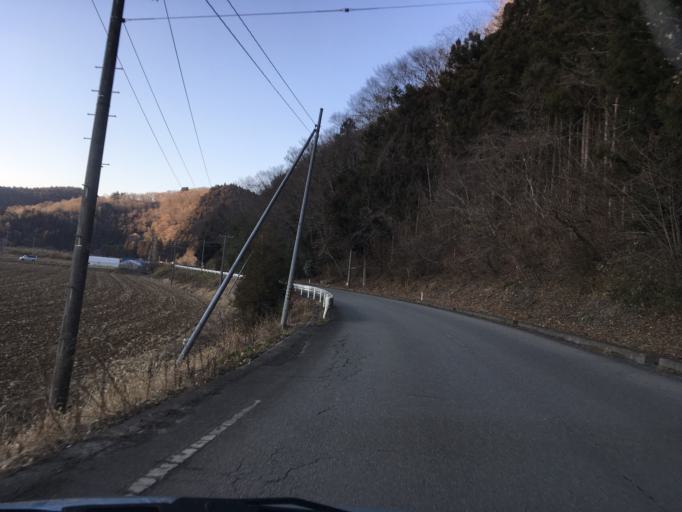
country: JP
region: Iwate
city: Ichinoseki
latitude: 38.7987
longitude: 141.2427
